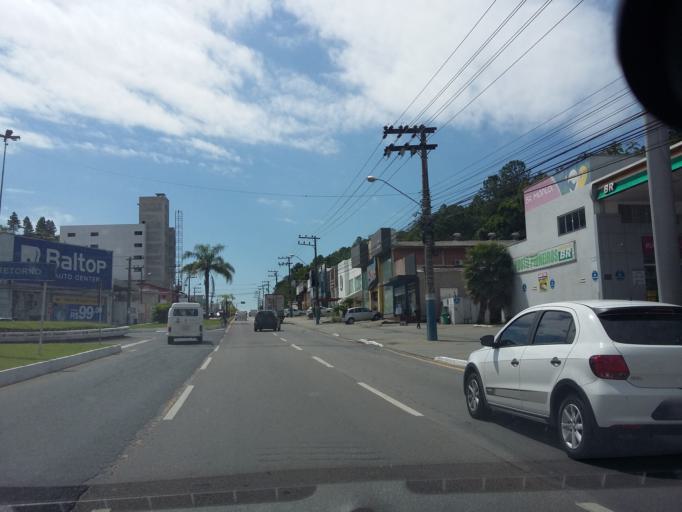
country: BR
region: Santa Catarina
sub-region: Balneario Camboriu
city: Balneario Camboriu
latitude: -26.9676
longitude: -48.6394
